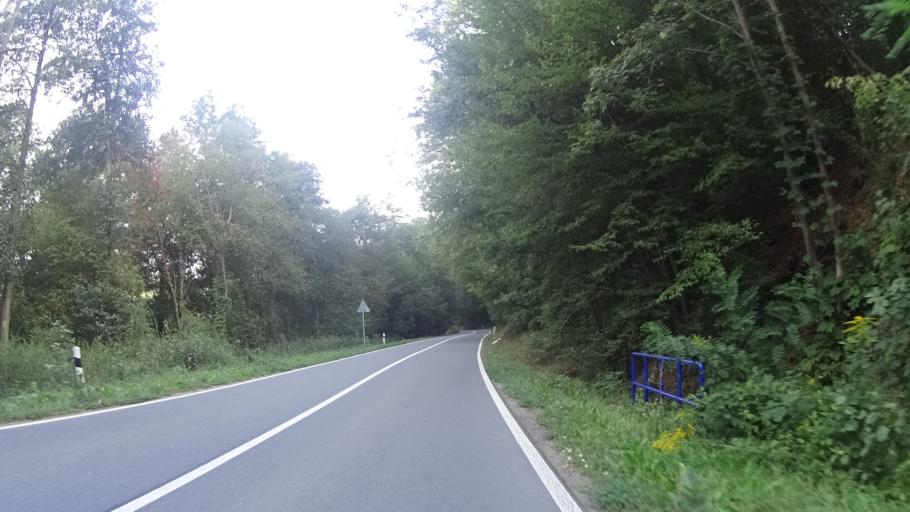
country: CZ
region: Olomoucky
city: Stity
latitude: 49.8650
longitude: 16.7374
